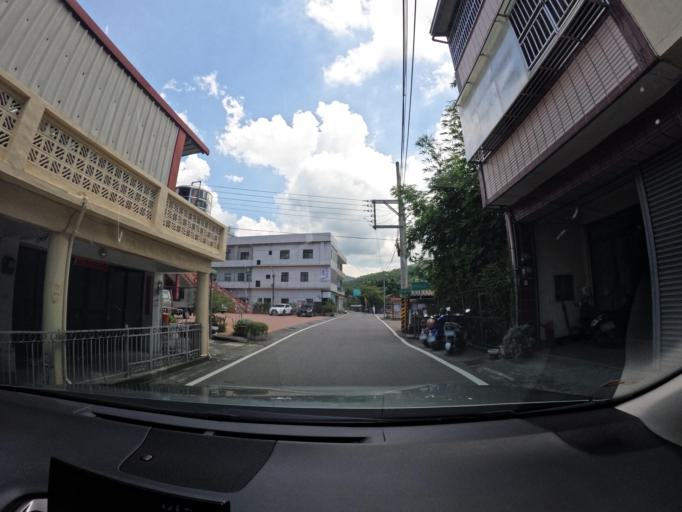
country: TW
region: Taiwan
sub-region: Miaoli
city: Miaoli
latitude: 24.4109
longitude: 120.7802
